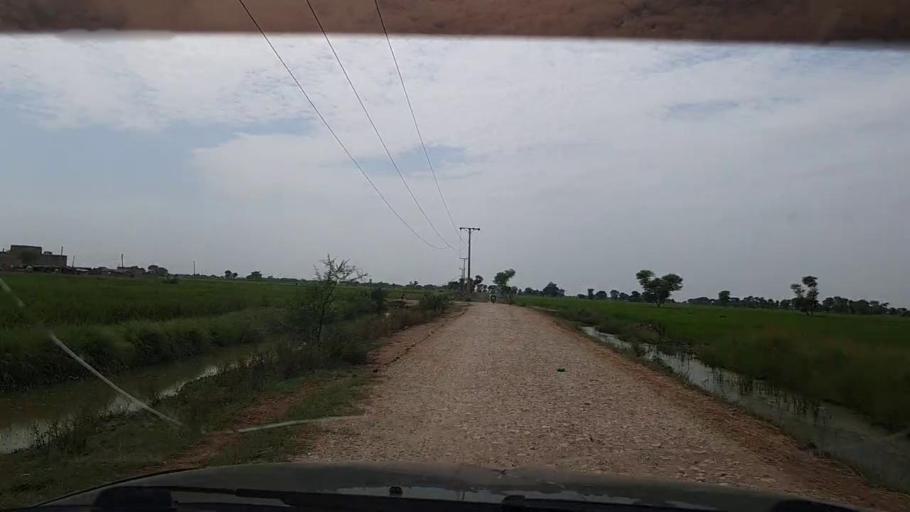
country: PK
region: Sindh
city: Thul
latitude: 28.2418
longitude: 68.7236
